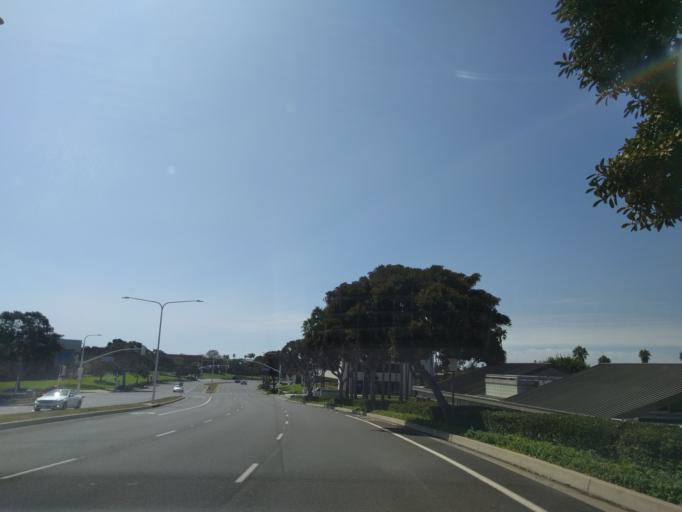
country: US
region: California
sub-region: Orange County
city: San Joaquin Hills
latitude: 33.6117
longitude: -117.8783
